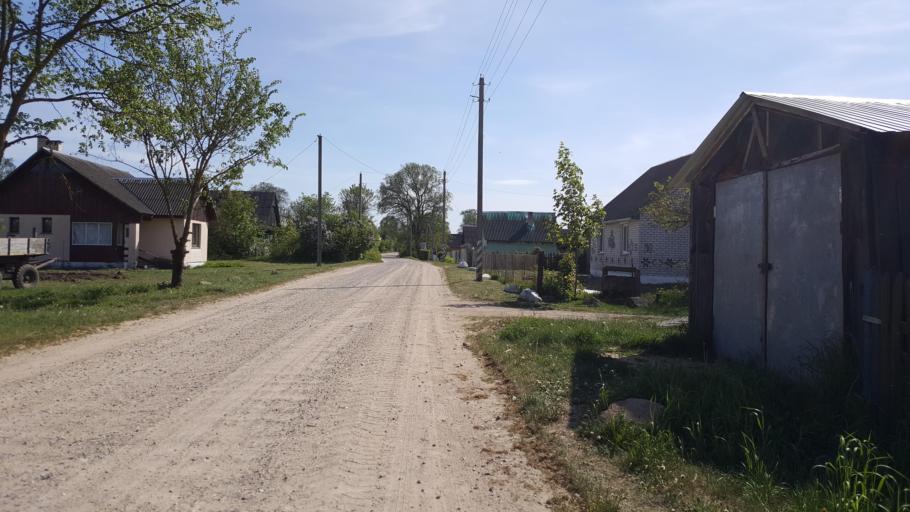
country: BY
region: Brest
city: Zhabinka
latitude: 52.3185
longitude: 24.0425
